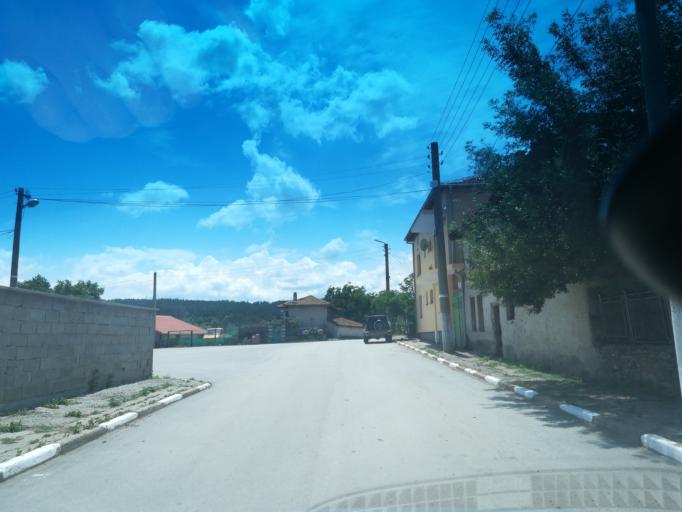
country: BG
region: Khaskovo
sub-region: Obshtina Mineralni Bani
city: Mineralni Bani
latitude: 41.9472
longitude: 25.2459
